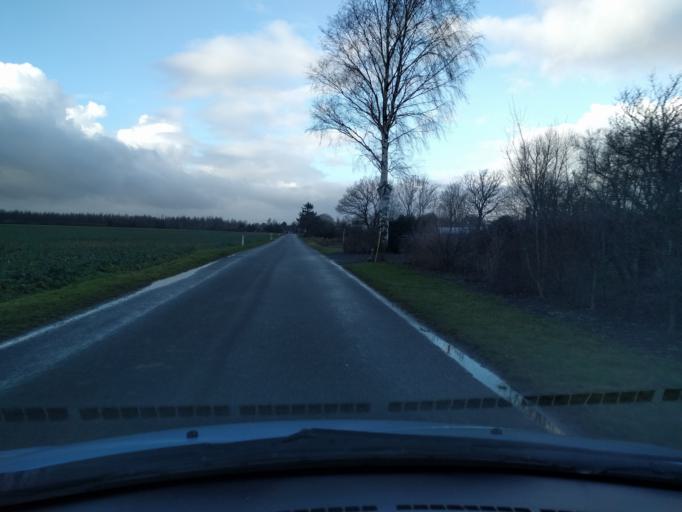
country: DK
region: South Denmark
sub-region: Kerteminde Kommune
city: Langeskov
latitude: 55.3912
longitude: 10.5692
